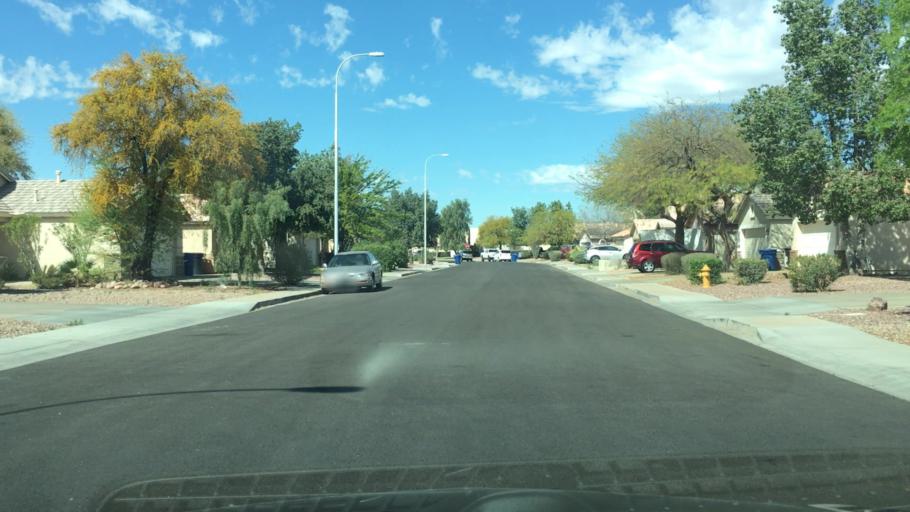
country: US
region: Arizona
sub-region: Maricopa County
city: Chandler
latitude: 33.3121
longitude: -111.8095
